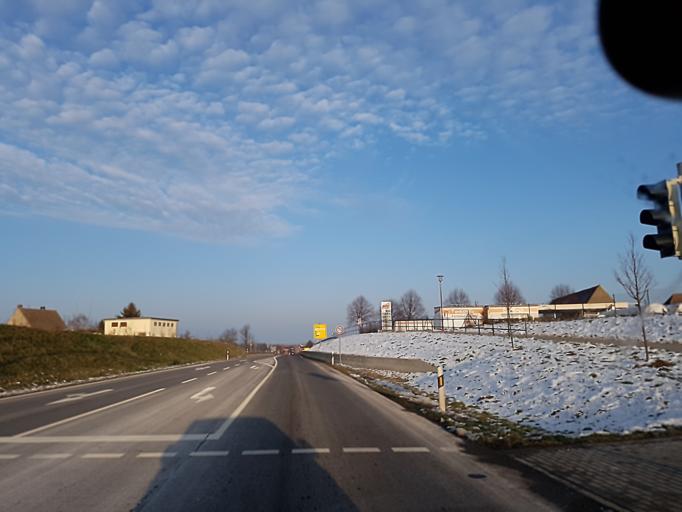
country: DE
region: Saxony
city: Mugeln
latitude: 51.2333
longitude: 13.0575
